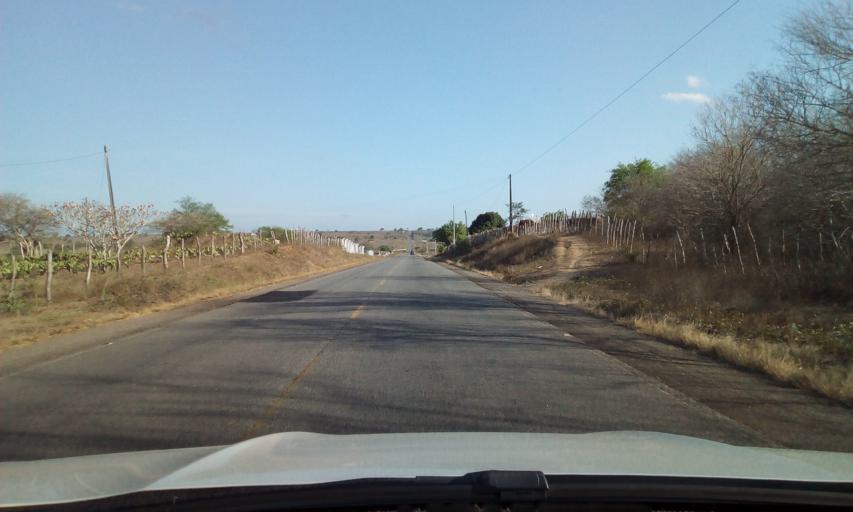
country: BR
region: Paraiba
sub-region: Mulungu
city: Mulungu
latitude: -6.9647
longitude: -35.4083
